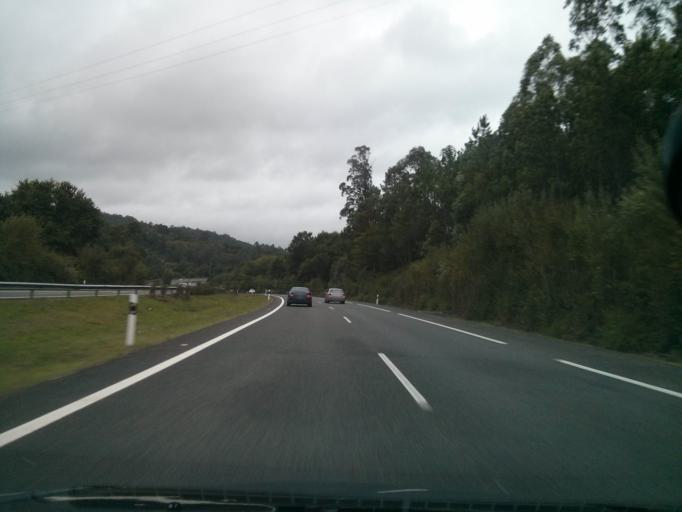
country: ES
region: Galicia
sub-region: Provincia de Pontevedra
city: Ponteareas
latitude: 42.1604
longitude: -8.5251
